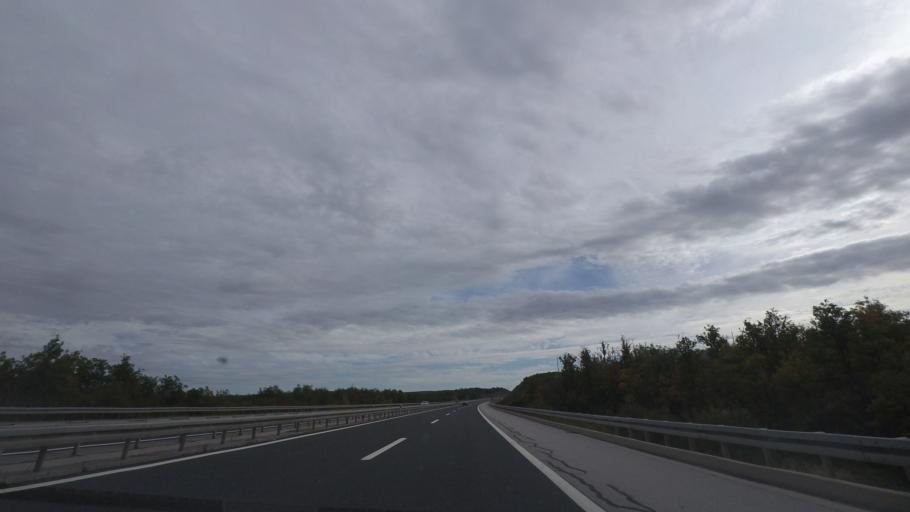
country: HR
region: Licko-Senjska
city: Gospic
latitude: 44.7288
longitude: 15.3841
